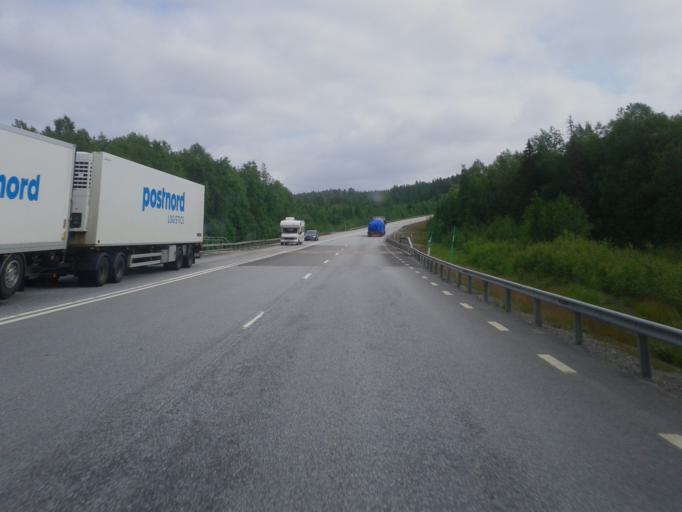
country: SE
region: Vaesterbotten
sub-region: Robertsfors Kommun
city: Robertsfors
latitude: 64.2928
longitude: 21.0823
